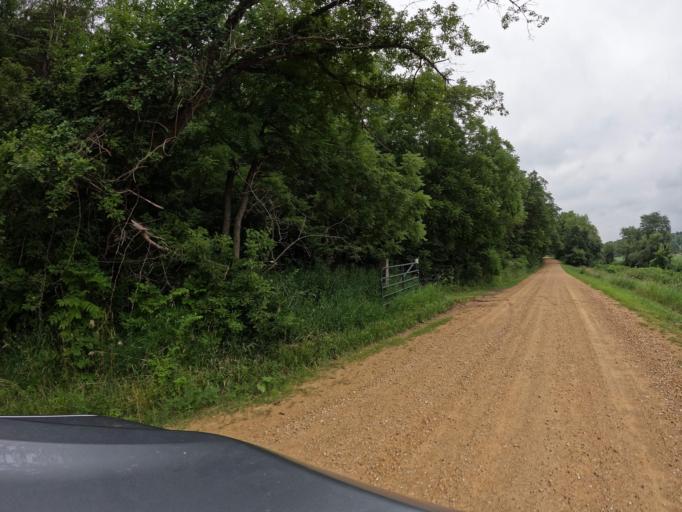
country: US
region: Illinois
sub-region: Carroll County
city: Savanna
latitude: 41.9888
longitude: -90.1735
